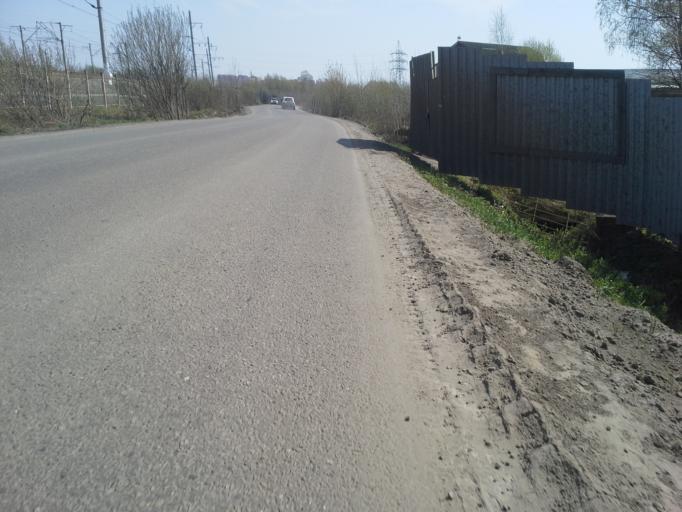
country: RU
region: Moskovskaya
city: Shcherbinka
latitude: 55.5162
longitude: 37.5370
